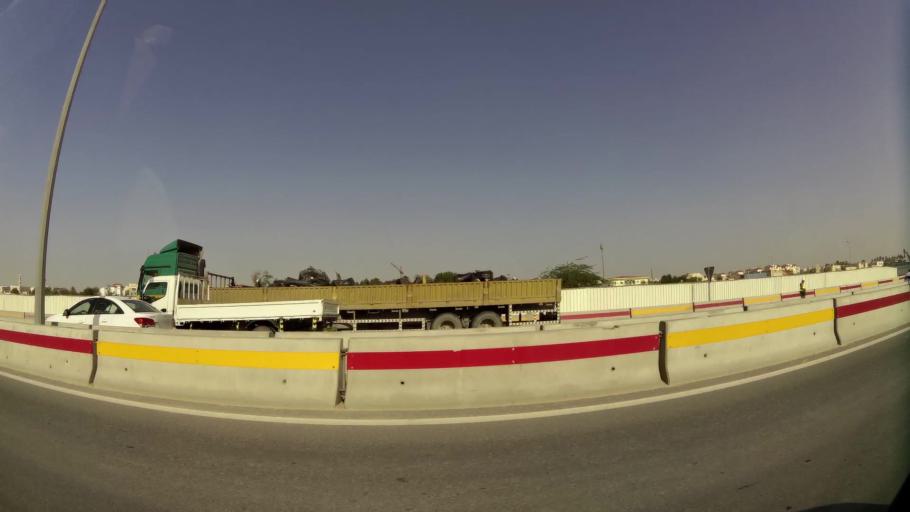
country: QA
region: Baladiyat ar Rayyan
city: Ar Rayyan
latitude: 25.3258
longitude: 51.4479
